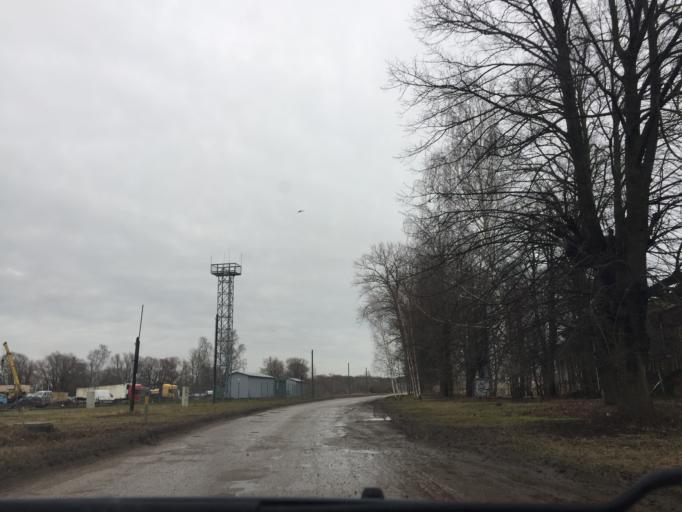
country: LV
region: Riga
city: Riga
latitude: 56.9780
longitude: 24.1233
